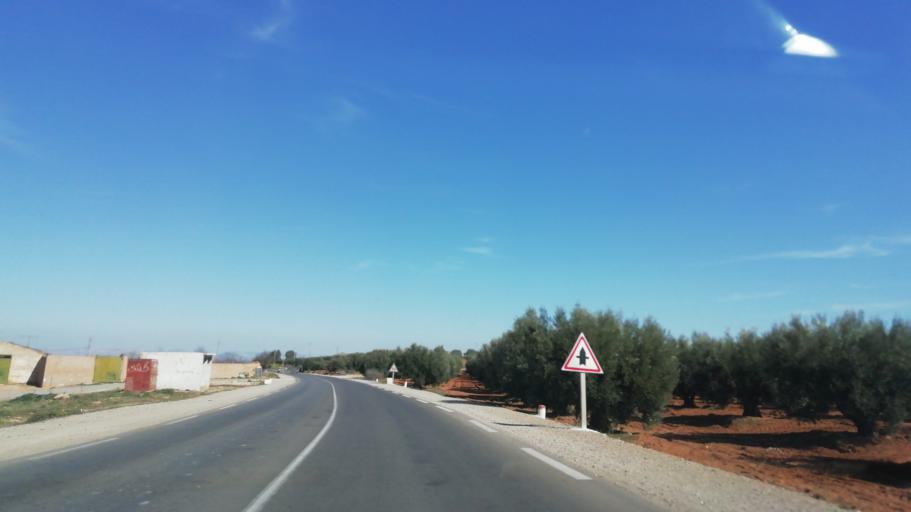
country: DZ
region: Mascara
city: Oued el Abtal
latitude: 35.4275
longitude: 0.4701
